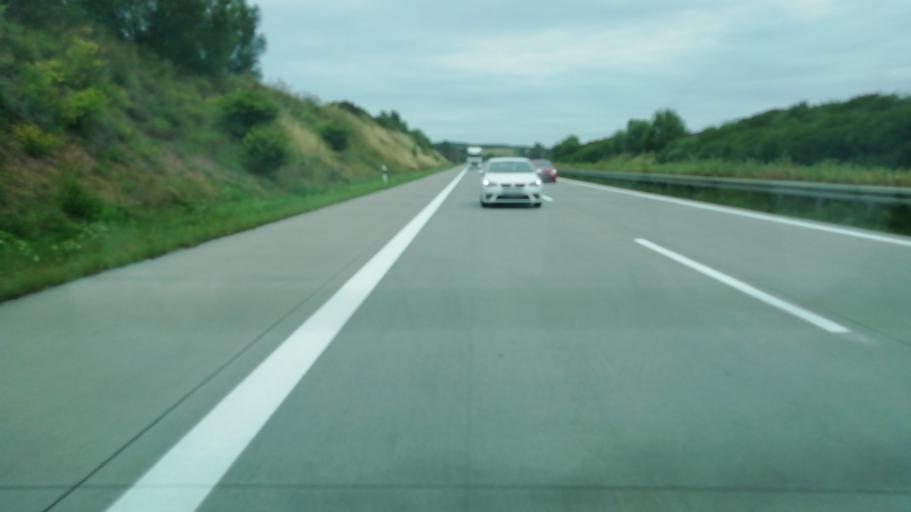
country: DE
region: Saxony
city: Niederdorf
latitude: 50.7645
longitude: 12.8105
